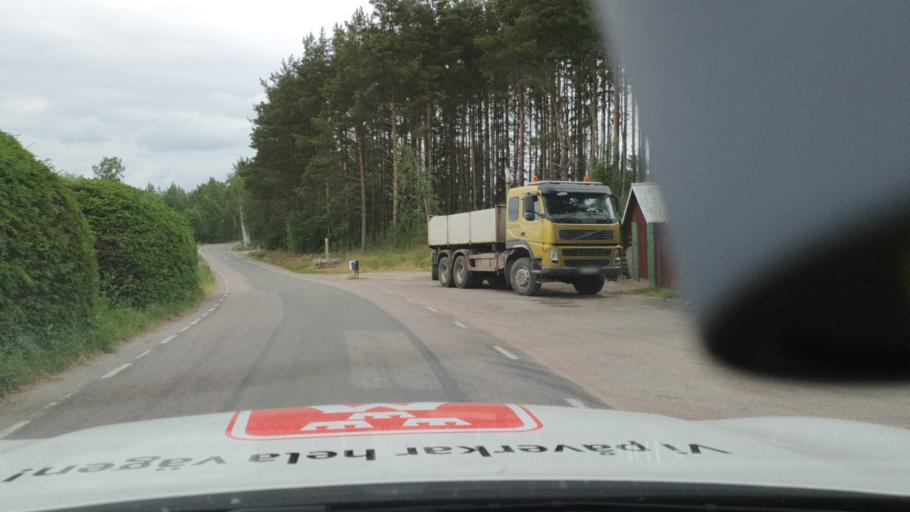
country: SE
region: Vaestra Goetaland
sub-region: Tidaholms Kommun
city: Olofstorp
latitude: 58.2384
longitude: 14.0978
